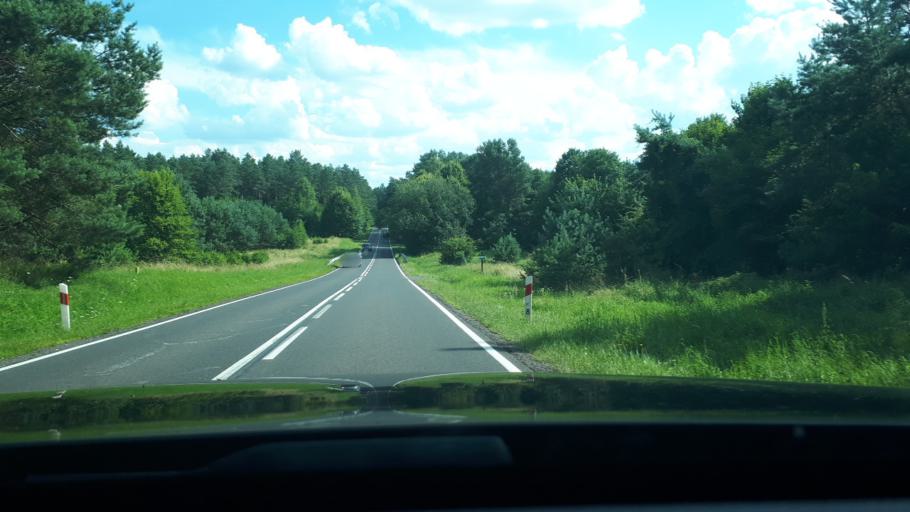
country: PL
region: Warmian-Masurian Voivodeship
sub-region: Powiat olsztynski
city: Stawiguda
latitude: 53.5453
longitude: 20.4195
